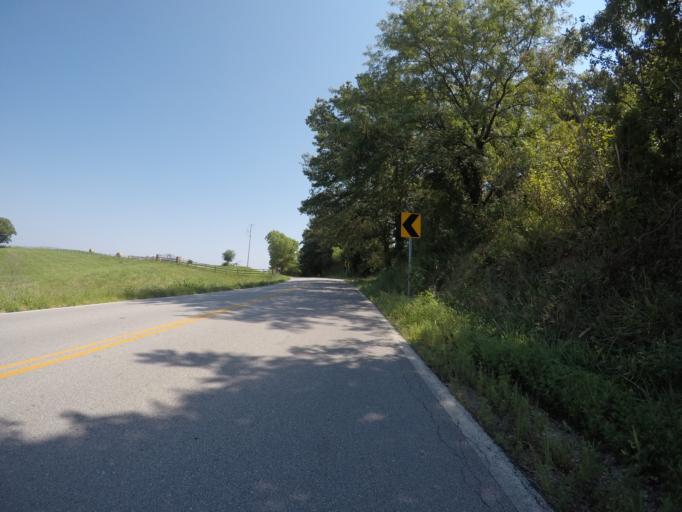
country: US
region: Kansas
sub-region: Leavenworth County
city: Lansing
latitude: 39.2103
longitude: -94.8372
